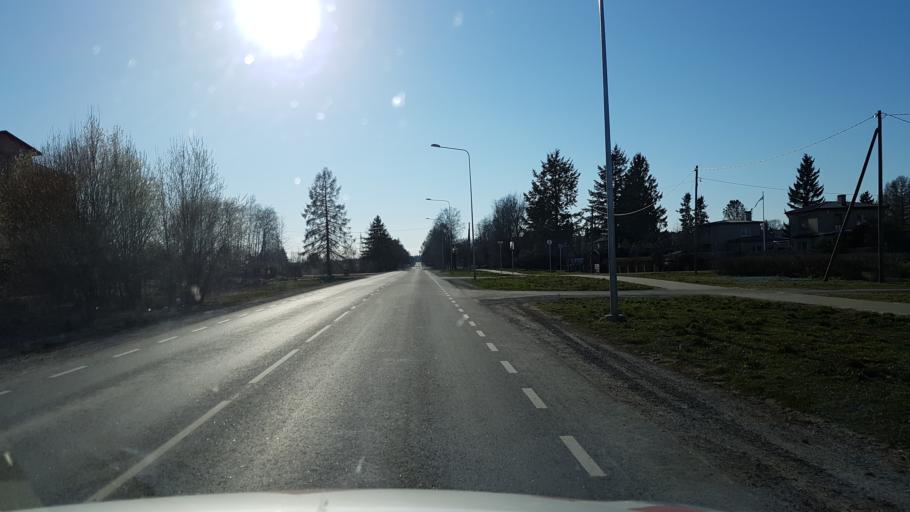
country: EE
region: Ida-Virumaa
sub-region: Johvi vald
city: Johvi
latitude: 59.3518
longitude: 27.4059
